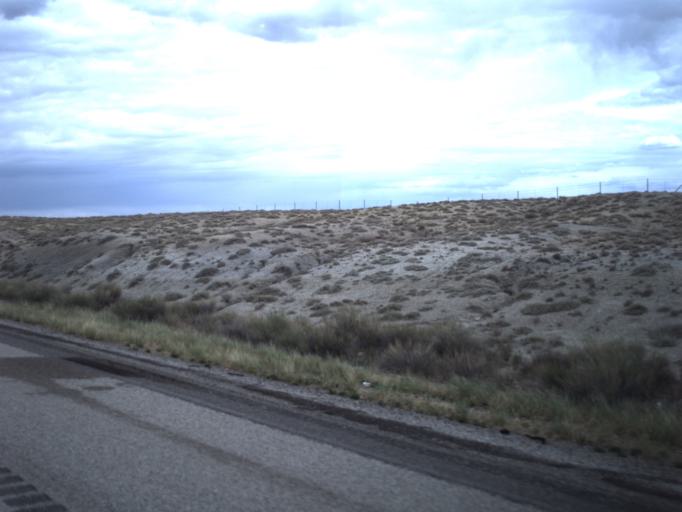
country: US
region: Utah
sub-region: Grand County
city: Moab
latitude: 38.9911
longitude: -109.3328
